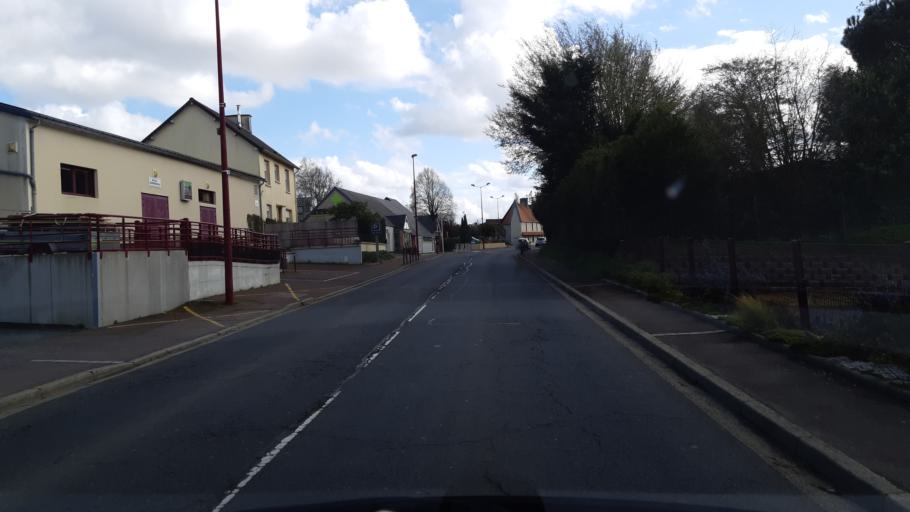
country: FR
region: Lower Normandy
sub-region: Departement de la Manche
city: Agneaux
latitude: 49.0467
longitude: -1.1281
